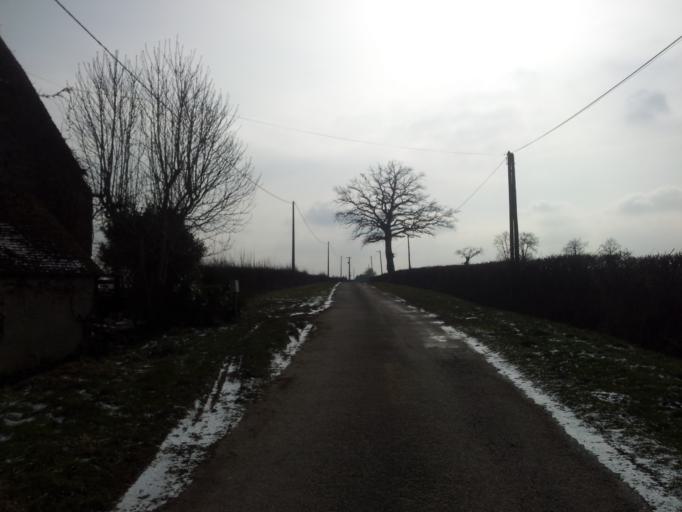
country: FR
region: Auvergne
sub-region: Departement de l'Allier
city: Chantelle
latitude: 46.3149
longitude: 3.0884
